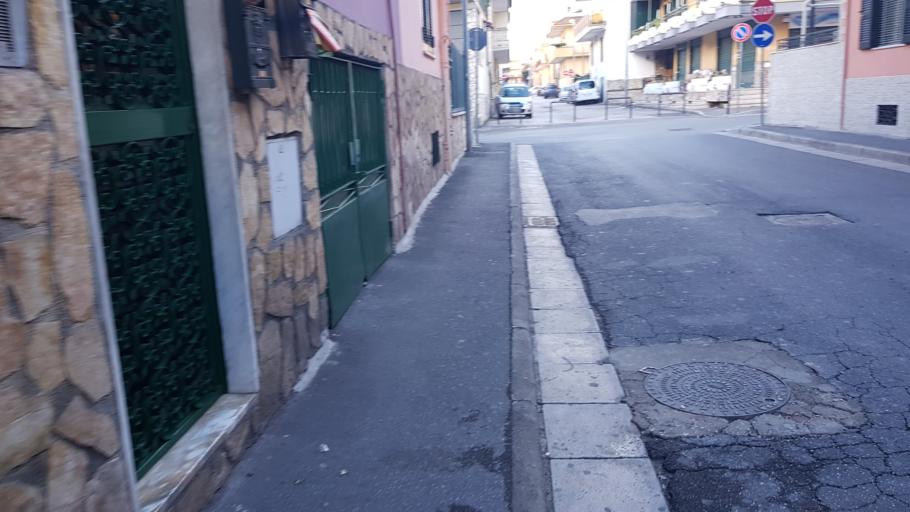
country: IT
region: Campania
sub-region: Provincia di Napoli
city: Mugnano di Napoli
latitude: 40.9076
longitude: 14.2102
